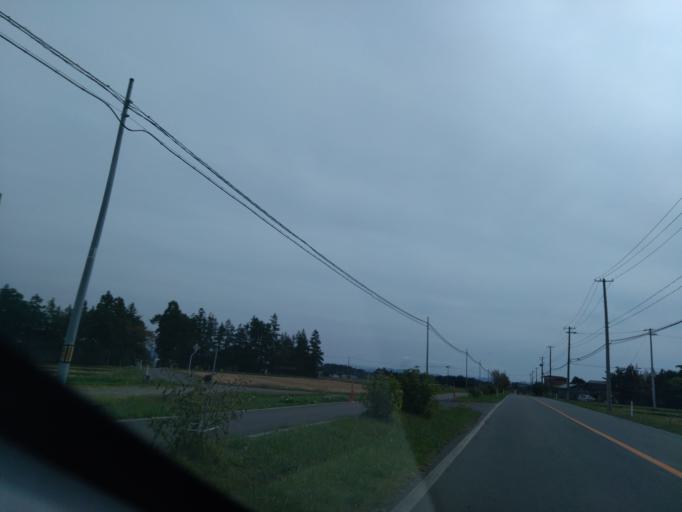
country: JP
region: Iwate
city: Hanamaki
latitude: 39.4338
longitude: 141.0826
